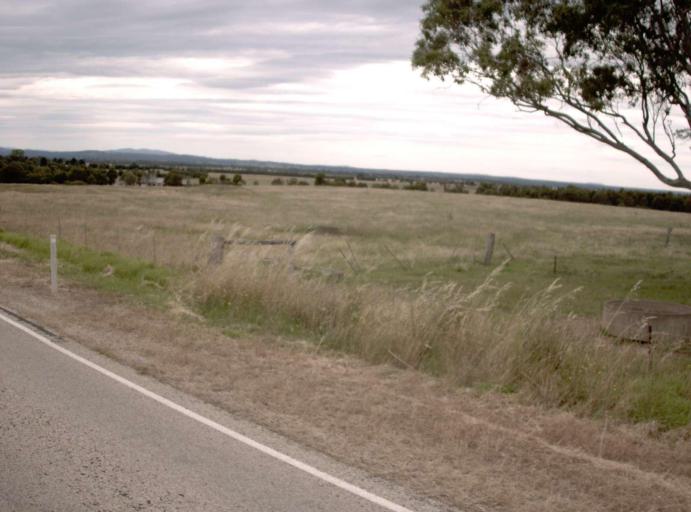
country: AU
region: Victoria
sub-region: East Gippsland
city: Bairnsdale
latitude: -37.8735
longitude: 147.5605
